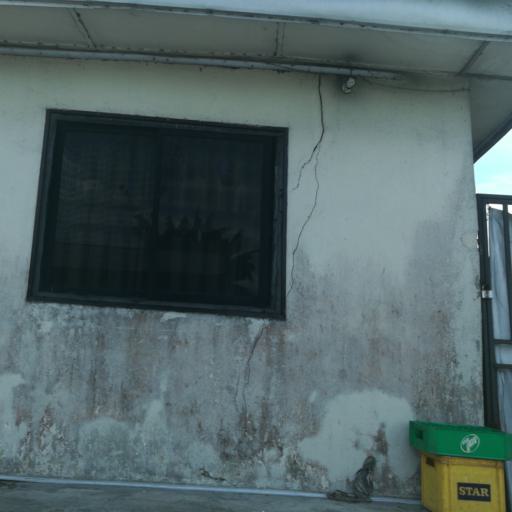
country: NG
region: Rivers
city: Port Harcourt
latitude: 4.7767
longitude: 7.0447
